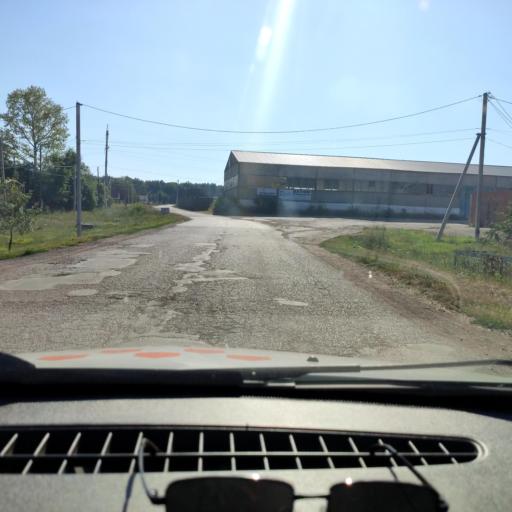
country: RU
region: Bashkortostan
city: Tolbazy
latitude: 54.0050
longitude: 55.8885
